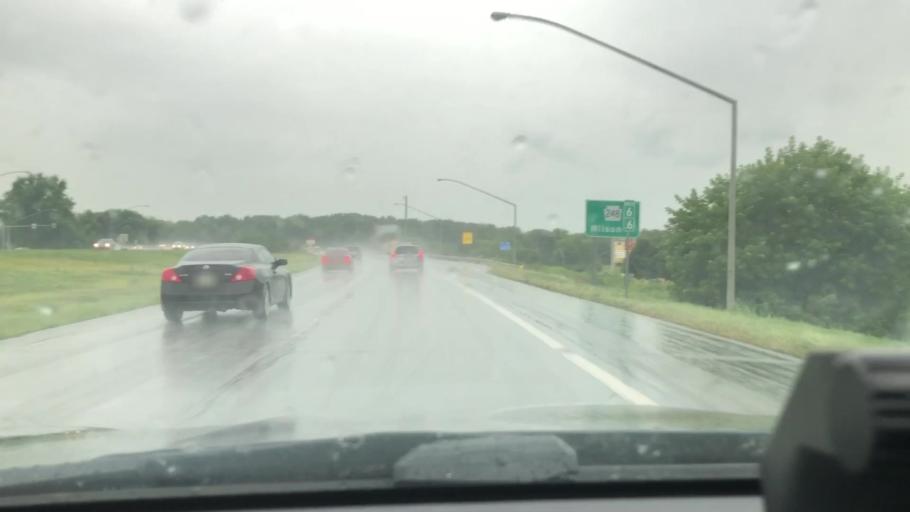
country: US
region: Pennsylvania
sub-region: Northampton County
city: Nazareth
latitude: 40.7192
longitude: -75.2869
